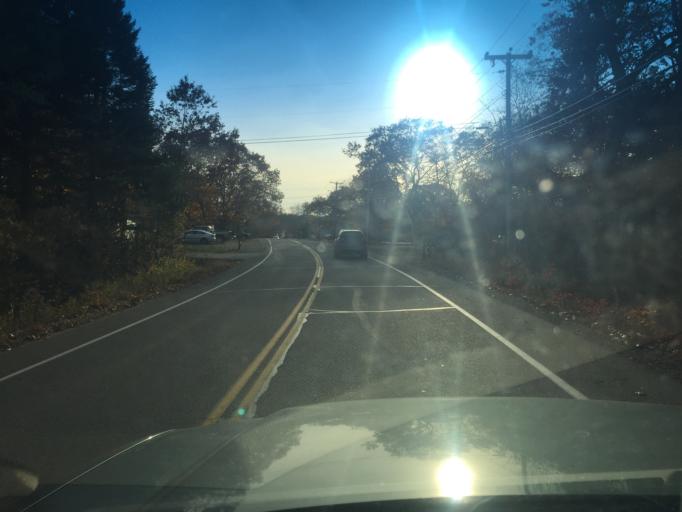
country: US
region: Maine
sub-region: York County
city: York Beach
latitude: 43.1712
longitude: -70.6186
